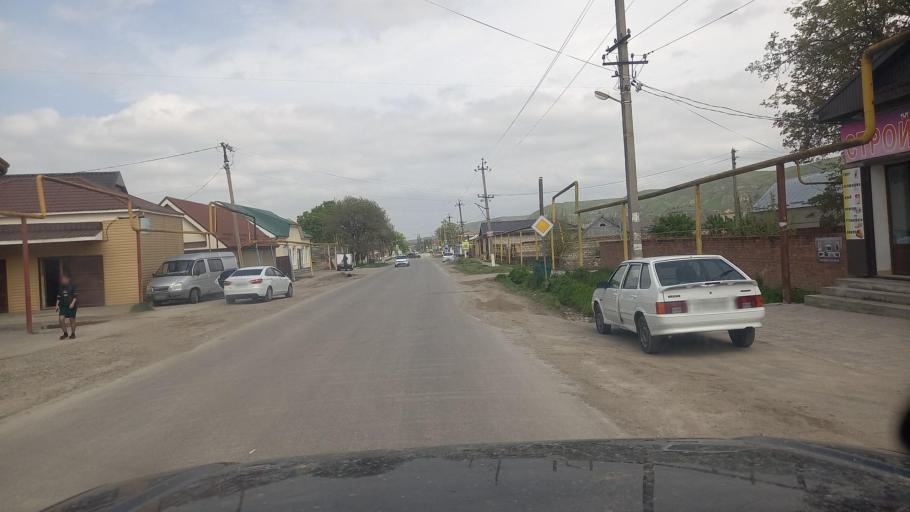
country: RU
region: Kabardino-Balkariya
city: Sarmakovo
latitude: 43.7434
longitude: 43.1975
